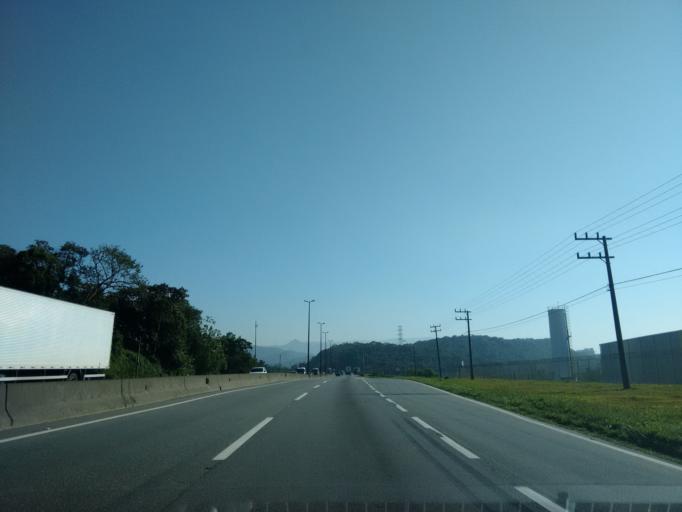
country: BR
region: Santa Catarina
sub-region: Joinville
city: Joinville
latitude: -26.2595
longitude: -48.9038
